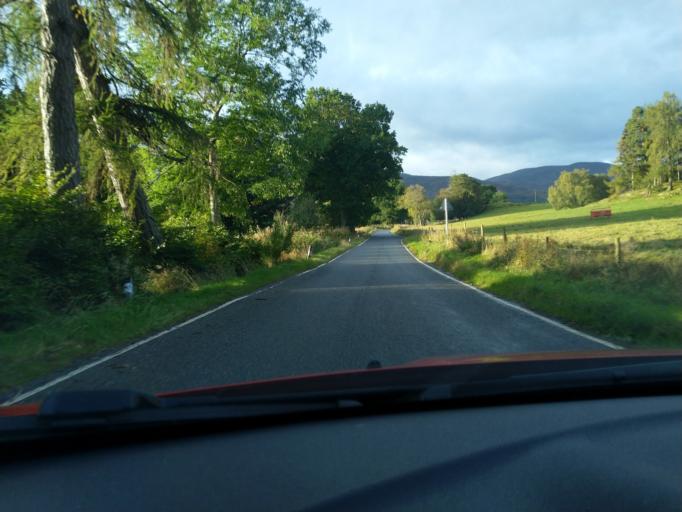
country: GB
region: Scotland
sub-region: Perth and Kinross
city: Aberfeldy
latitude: 56.7065
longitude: -4.1232
